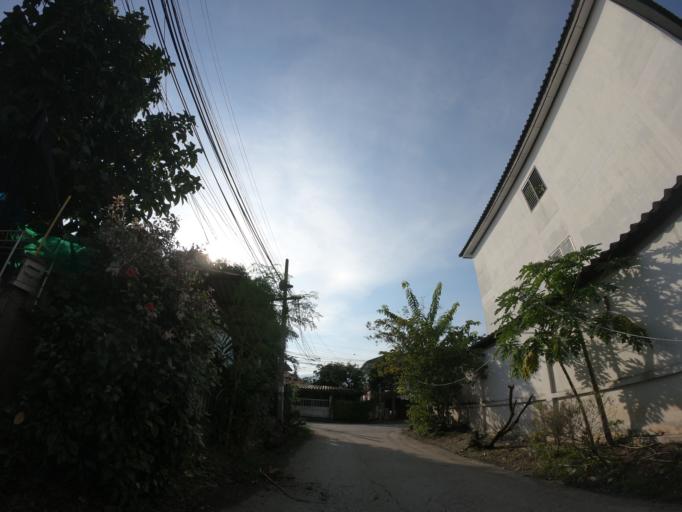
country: TH
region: Chiang Mai
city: Chiang Mai
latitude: 18.8280
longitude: 98.9884
